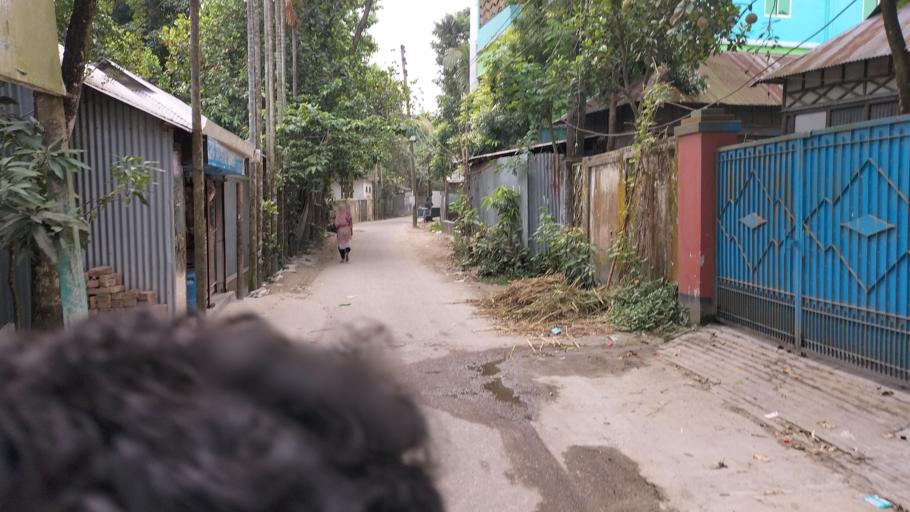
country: BD
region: Dhaka
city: Azimpur
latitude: 23.6822
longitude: 90.3155
